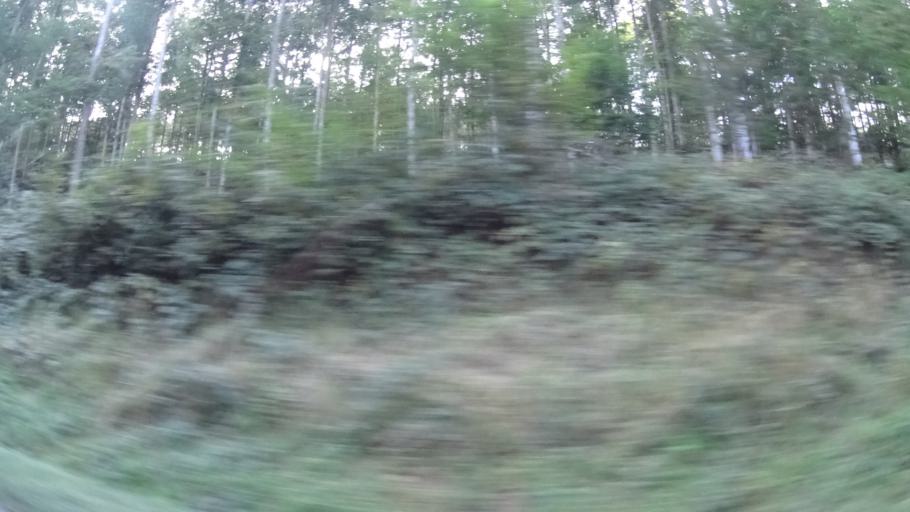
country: DE
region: Hesse
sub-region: Regierungsbezirk Darmstadt
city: Gelnhausen
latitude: 50.2698
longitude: 9.2162
